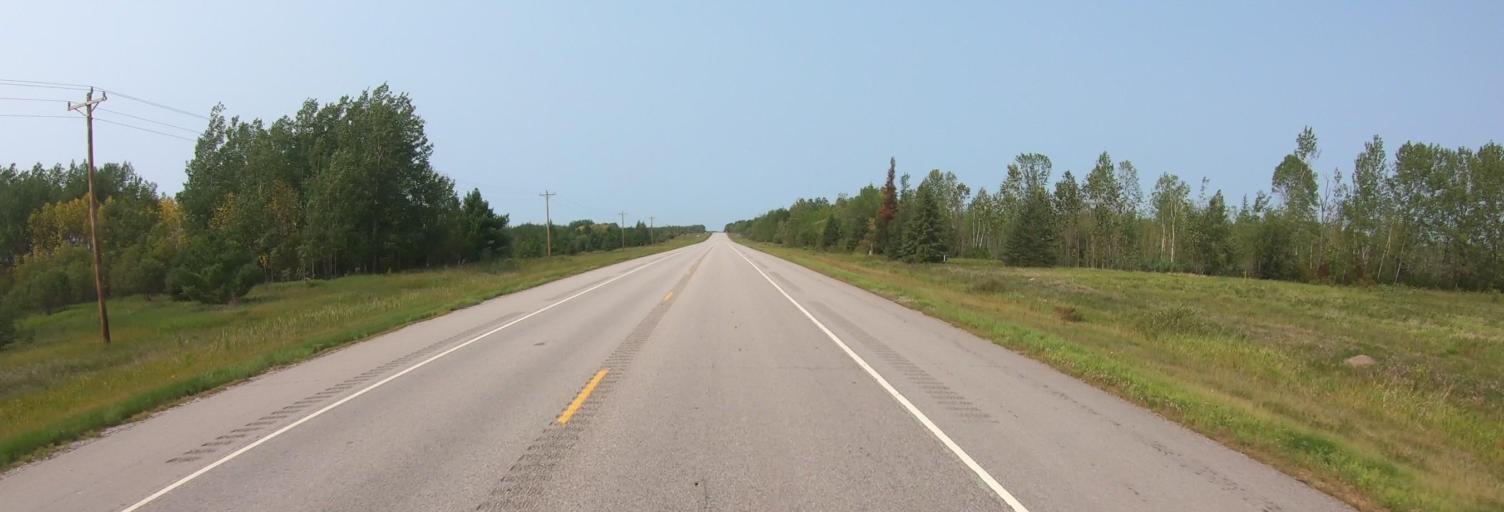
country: CA
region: Ontario
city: Fort Frances
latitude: 48.4101
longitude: -93.1470
